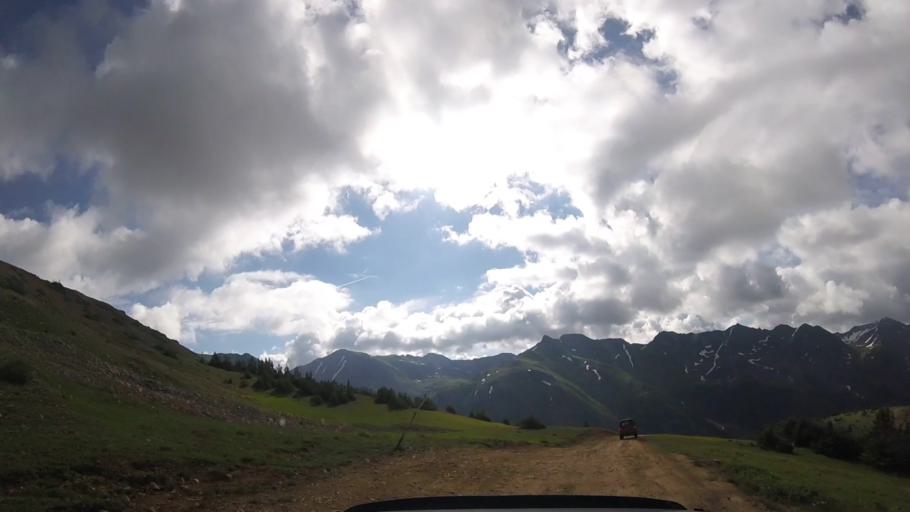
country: US
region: Colorado
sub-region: San Juan County
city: Silverton
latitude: 37.9066
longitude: -107.6592
